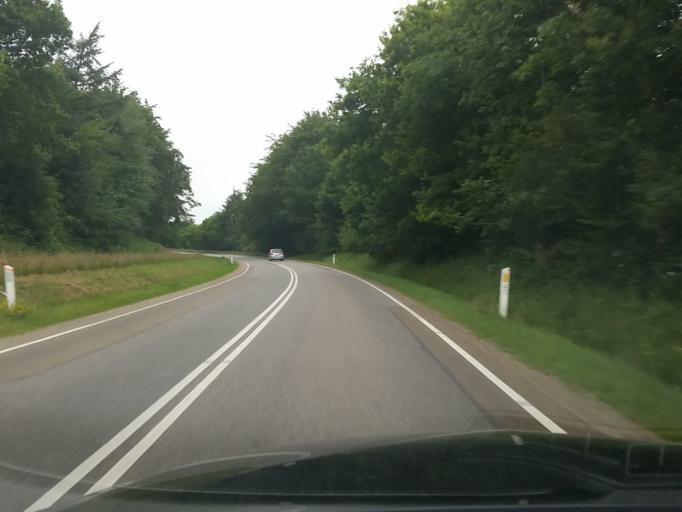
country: DK
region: South Denmark
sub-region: Billund Kommune
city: Grindsted
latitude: 55.6546
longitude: 8.8107
